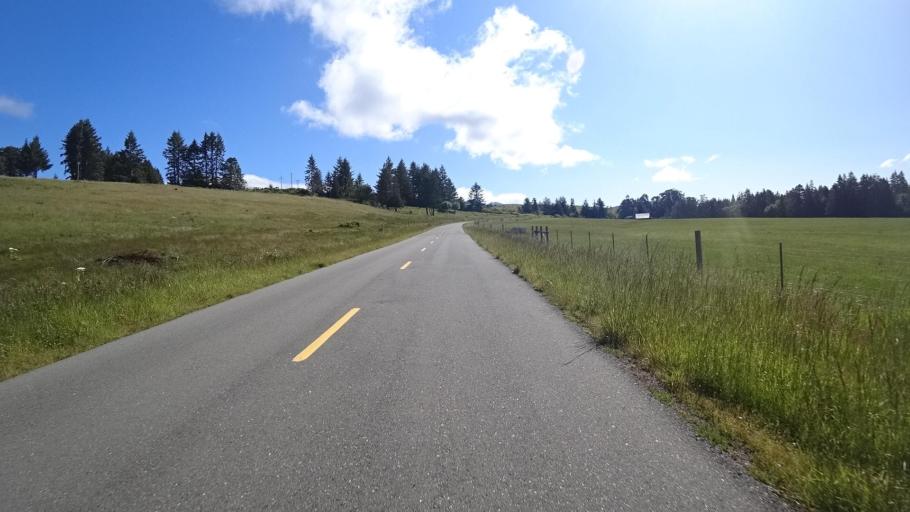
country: US
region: California
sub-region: Humboldt County
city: Ferndale
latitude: 40.3472
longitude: -124.3343
